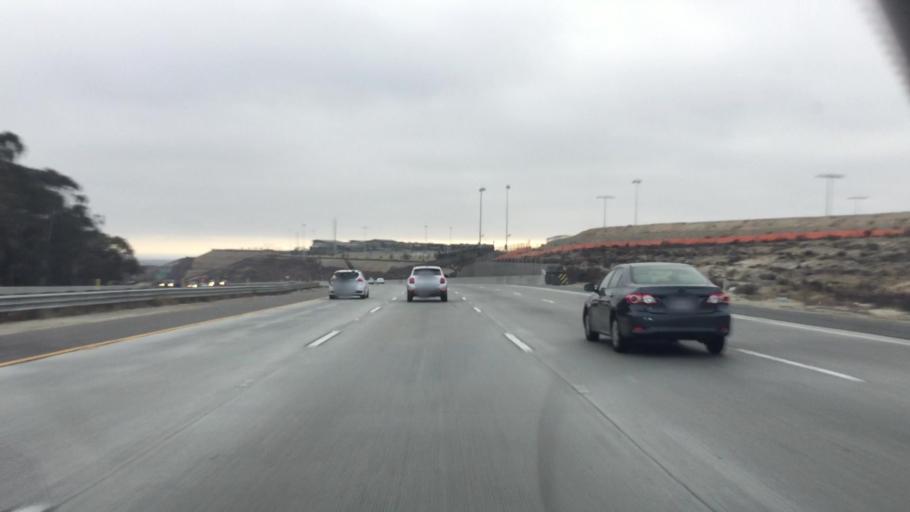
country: MX
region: Baja California
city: Tijuana
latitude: 32.5682
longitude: -117.0198
